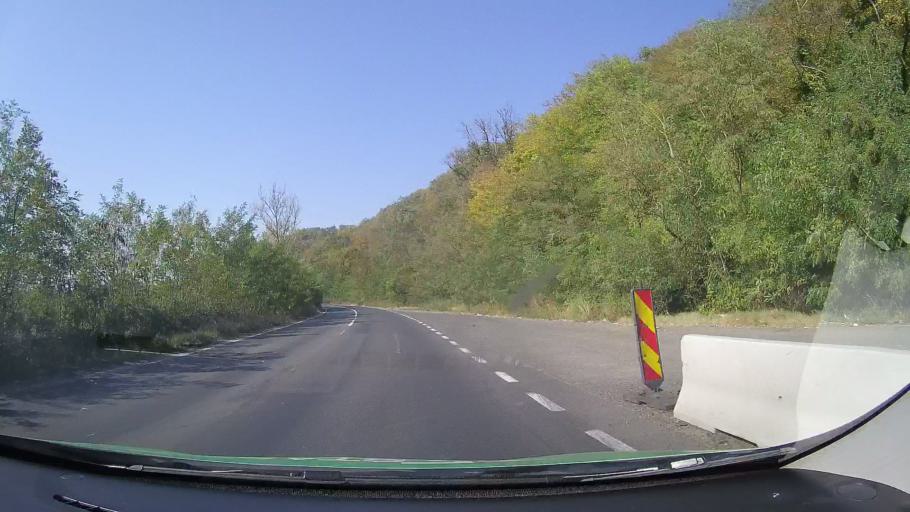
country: RO
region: Arad
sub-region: Comuna Savarsin
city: Savarsin
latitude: 46.0158
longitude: 22.2537
